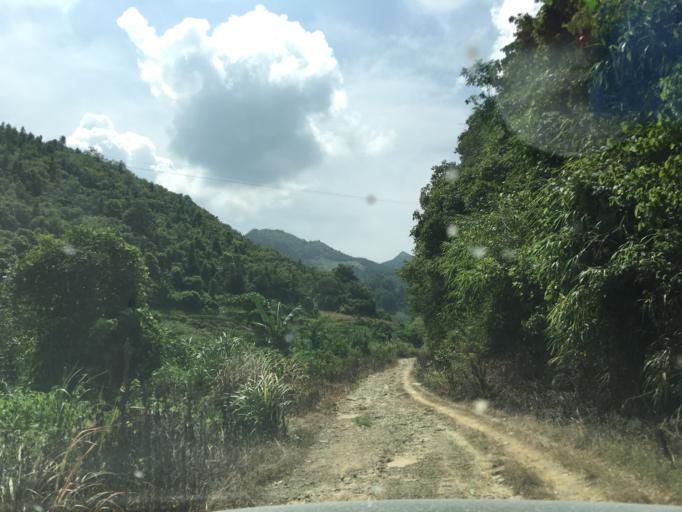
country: CN
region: Guangxi Zhuangzu Zizhiqu
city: Xinzhou
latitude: 24.9535
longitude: 105.7927
